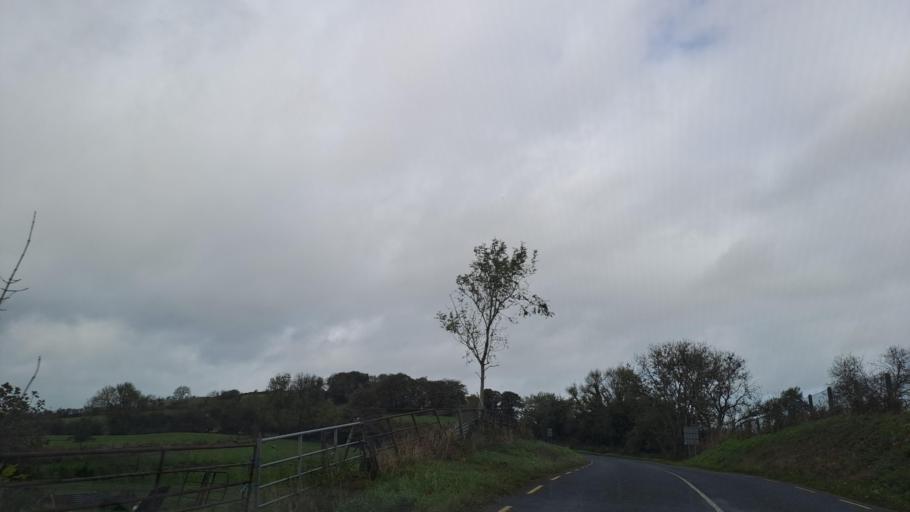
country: IE
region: Ulster
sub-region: An Cabhan
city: Bailieborough
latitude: 53.9215
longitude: -6.9486
